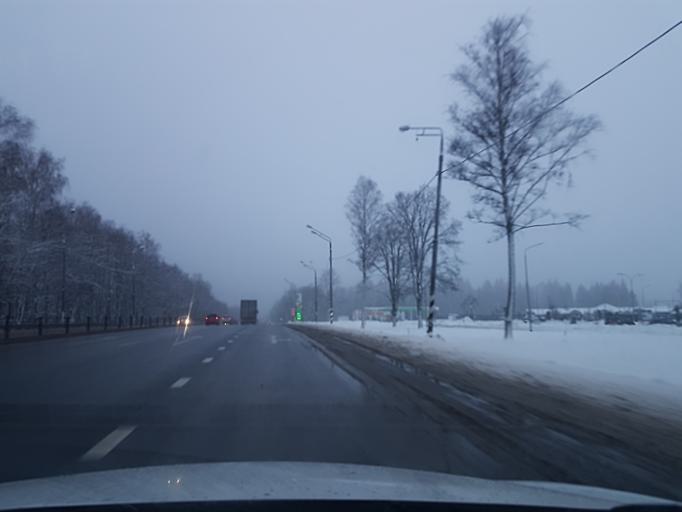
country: RU
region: Moskovskaya
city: Solnechnogorsk
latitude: 56.2024
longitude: 36.9540
